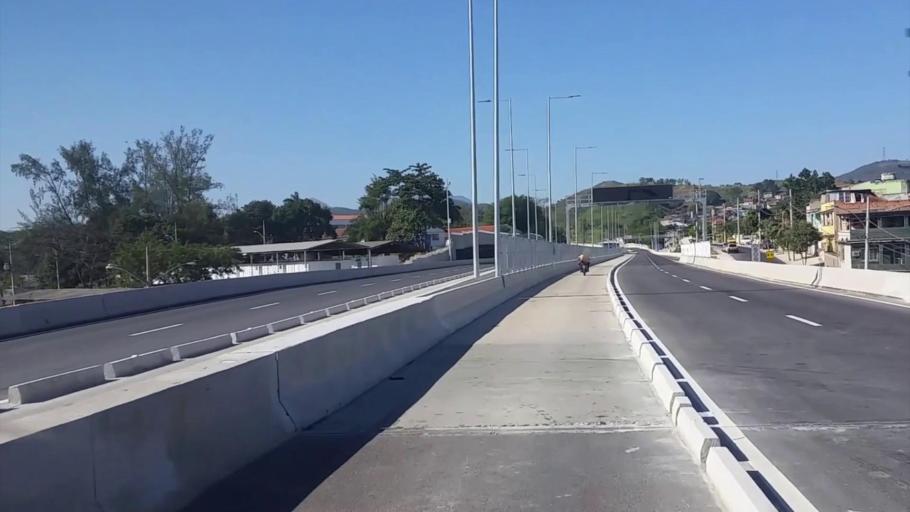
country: BR
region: Rio de Janeiro
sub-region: Nilopolis
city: Nilopolis
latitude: -22.8733
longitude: -43.4077
